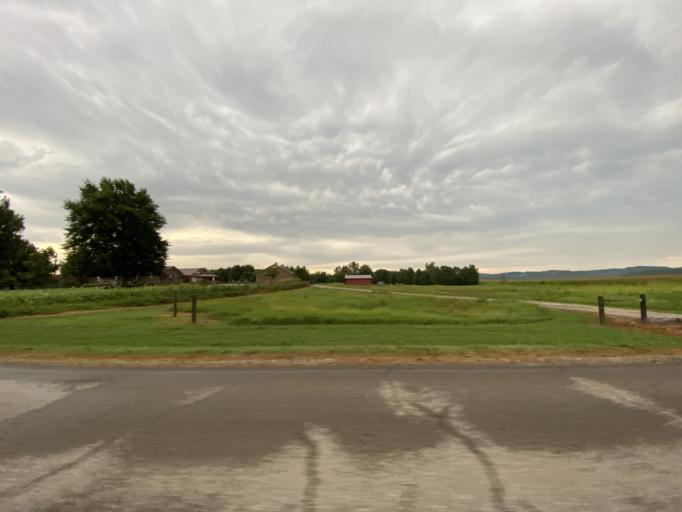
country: US
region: Alabama
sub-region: Lawrence County
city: Moulton
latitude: 34.4642
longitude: -87.5030
